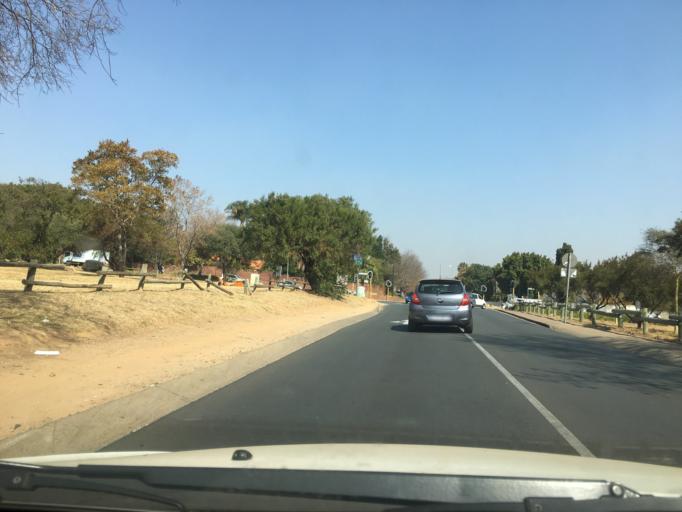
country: ZA
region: Gauteng
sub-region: City of Johannesburg Metropolitan Municipality
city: Midrand
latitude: -26.0748
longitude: 28.0465
